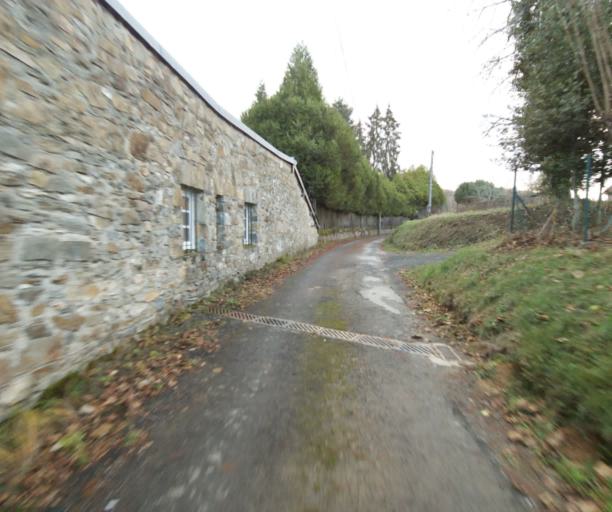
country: FR
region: Limousin
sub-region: Departement de la Correze
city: Laguenne
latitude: 45.2296
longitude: 1.7799
